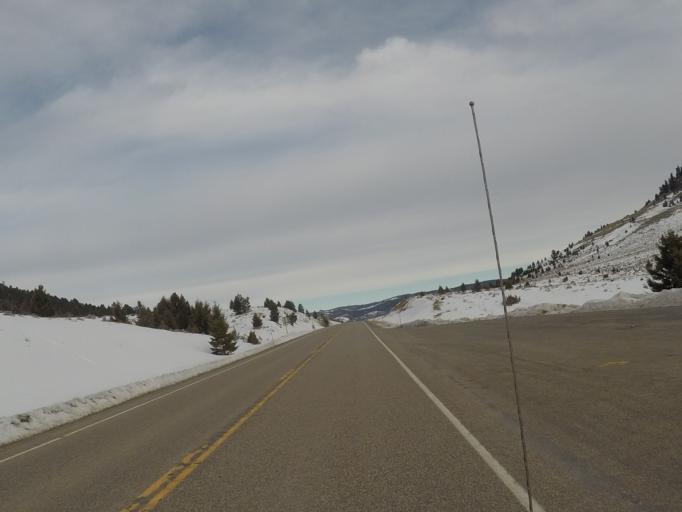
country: US
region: Montana
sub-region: Meagher County
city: White Sulphur Springs
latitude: 46.6433
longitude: -110.8641
